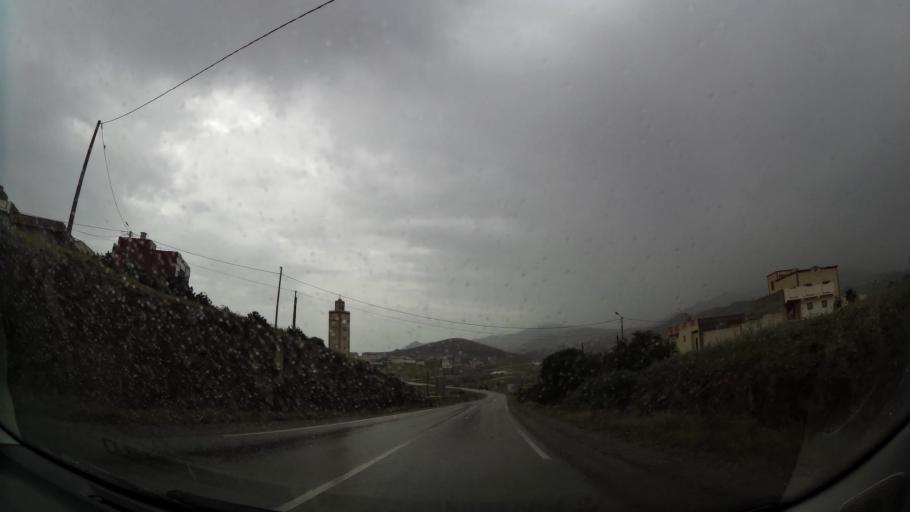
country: MA
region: Oriental
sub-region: Nador
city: Nador
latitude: 35.1467
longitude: -3.0161
